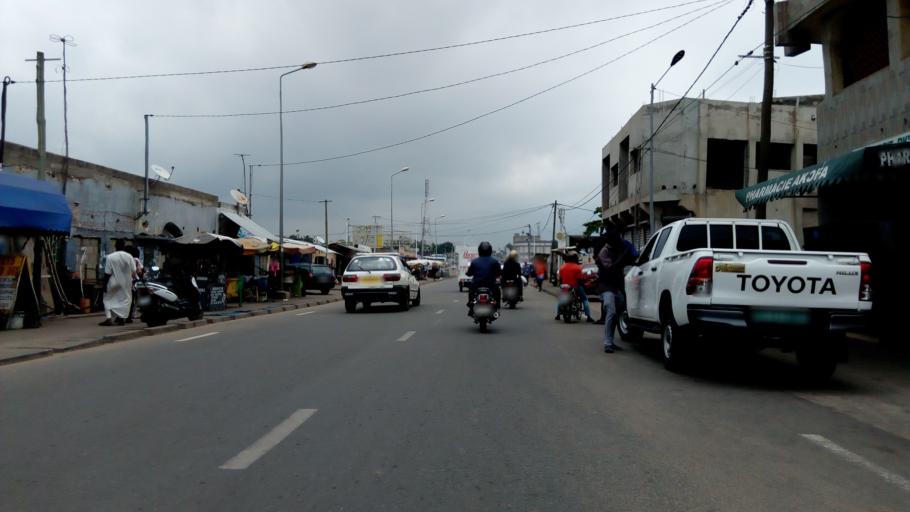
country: TG
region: Maritime
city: Lome
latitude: 6.1430
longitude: 1.2298
